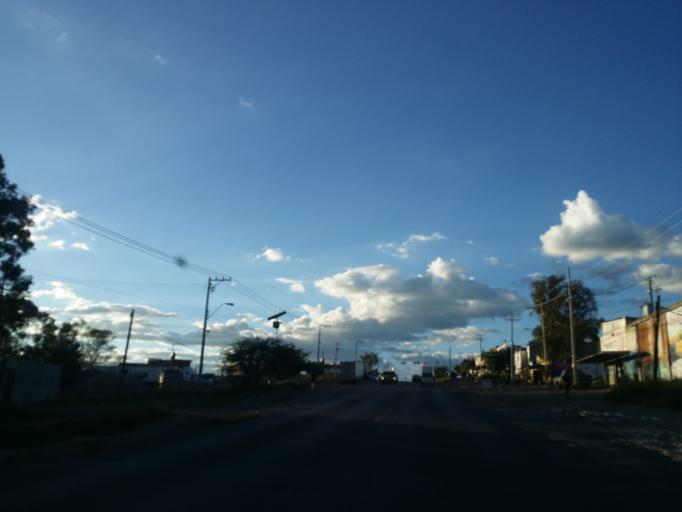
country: MX
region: Guanajuato
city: Leon
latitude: 21.2031
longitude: -101.6759
